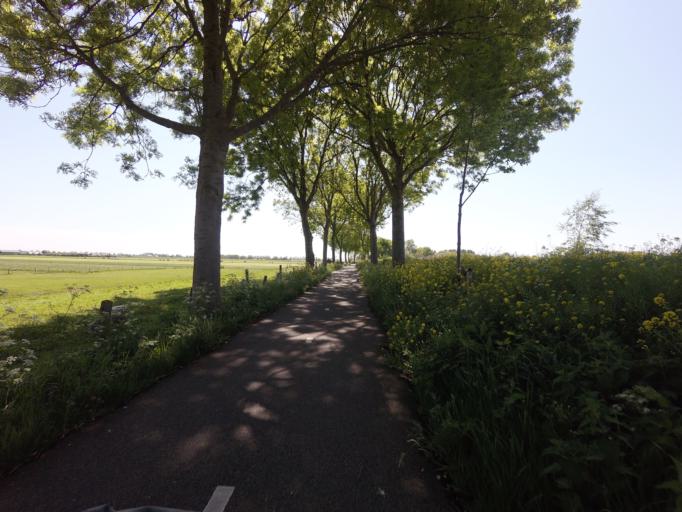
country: NL
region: North Holland
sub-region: Gemeente Uithoorn
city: Uithoorn
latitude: 52.2197
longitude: 4.8285
